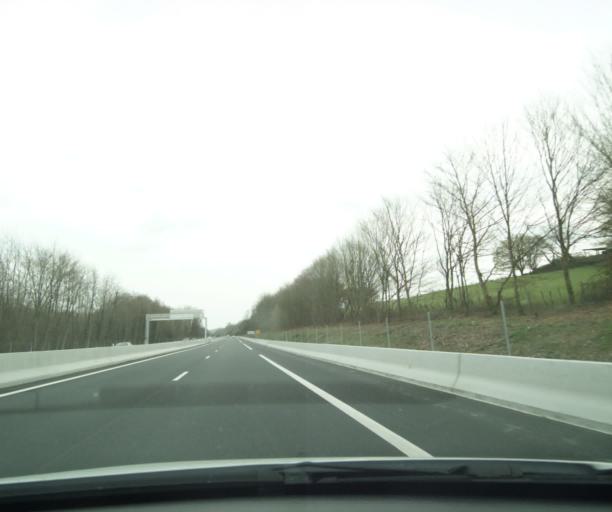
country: FR
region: Aquitaine
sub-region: Departement des Pyrenees-Atlantiques
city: Mouguerre
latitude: 43.4545
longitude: -1.3992
